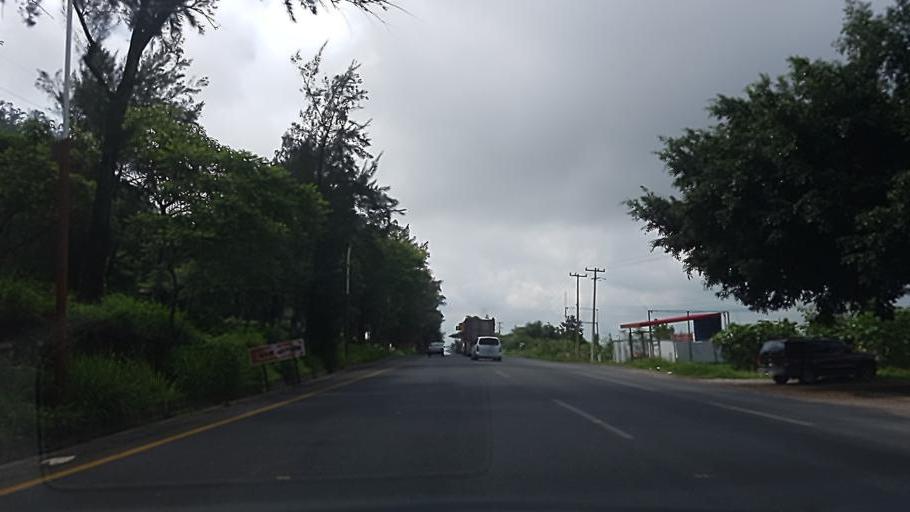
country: MX
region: Nayarit
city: Tepic
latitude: 21.5061
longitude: -104.9211
